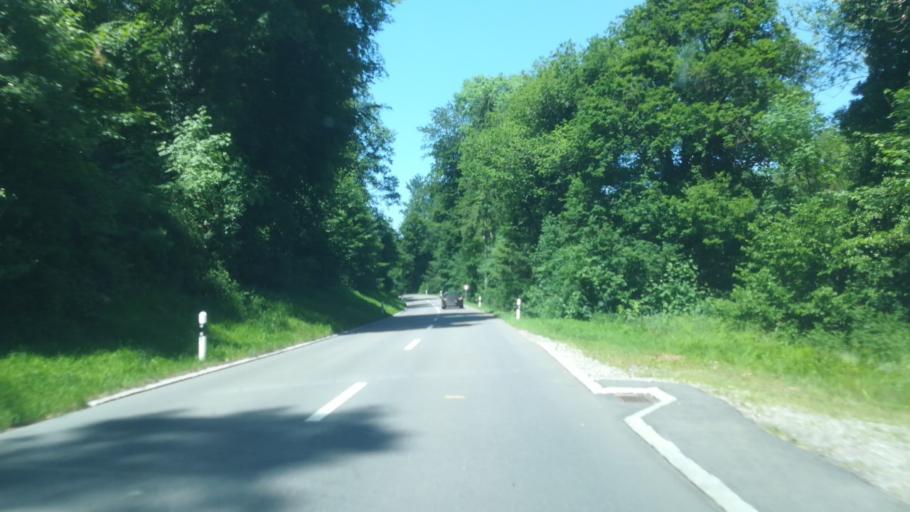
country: CH
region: Thurgau
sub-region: Frauenfeld District
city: Pfyn
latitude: 47.6331
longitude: 8.9233
